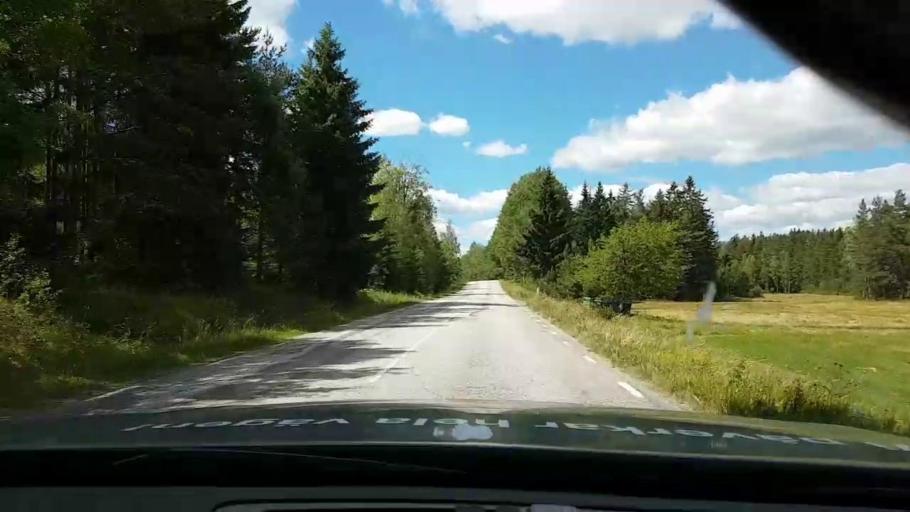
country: SE
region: Kalmar
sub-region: Vasterviks Kommun
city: Forserum
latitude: 58.0255
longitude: 16.5542
